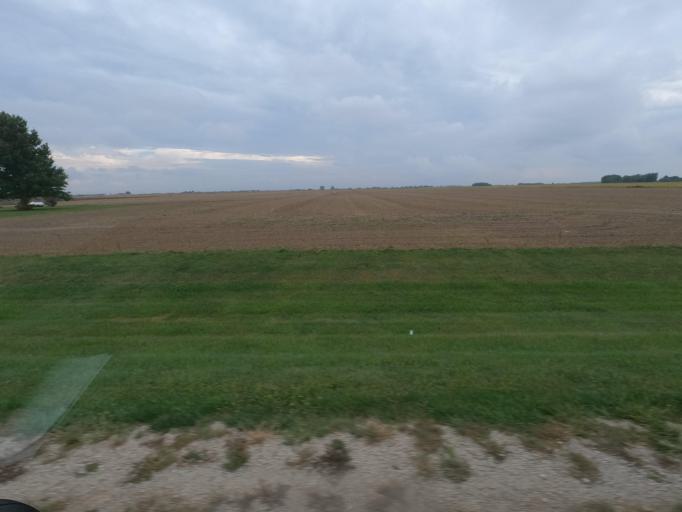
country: US
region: Iowa
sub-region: Van Buren County
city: Keosauqua
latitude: 40.8135
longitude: -91.8266
